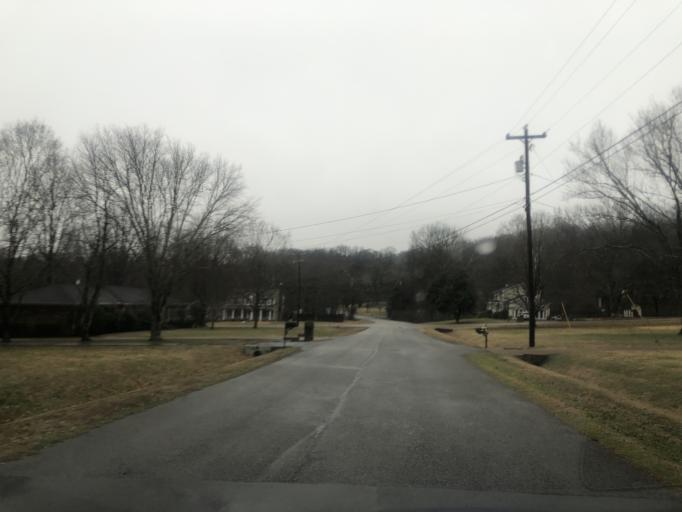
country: US
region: Tennessee
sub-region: Davidson County
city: Belle Meade
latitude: 36.0877
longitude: -86.9510
